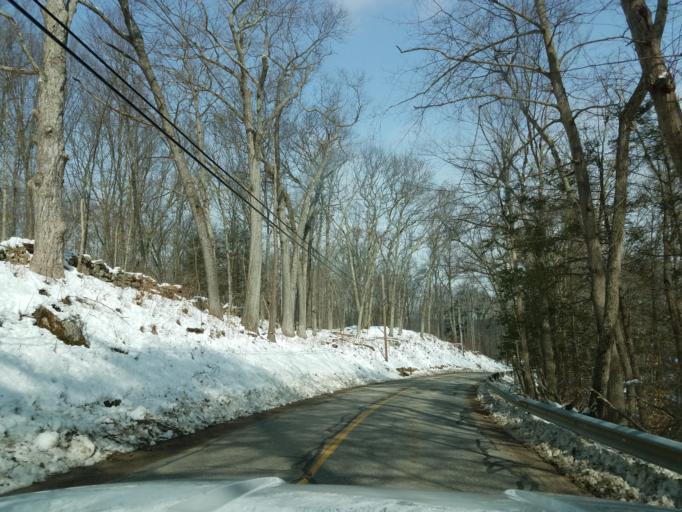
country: US
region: Connecticut
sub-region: Tolland County
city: Coventry Lake
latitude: 41.7289
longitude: -72.3586
